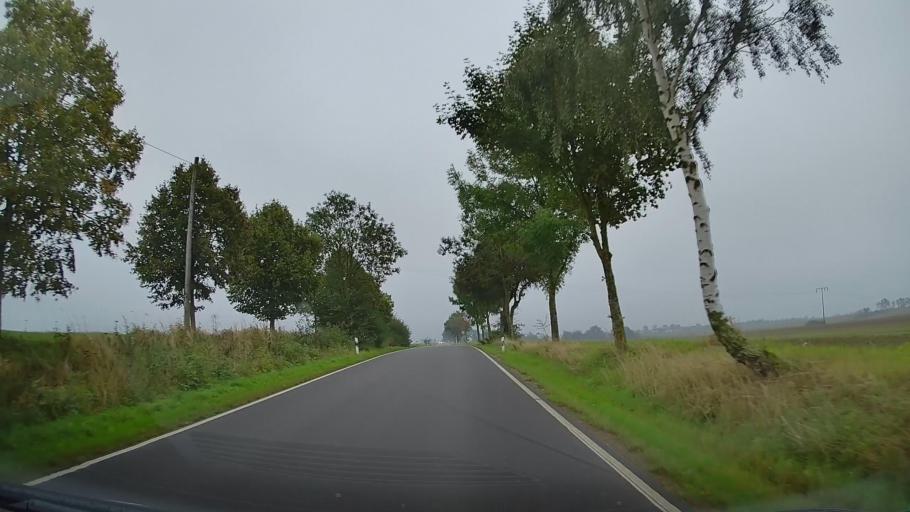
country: DE
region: Mecklenburg-Vorpommern
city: Gramkow
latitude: 53.9193
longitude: 11.3875
